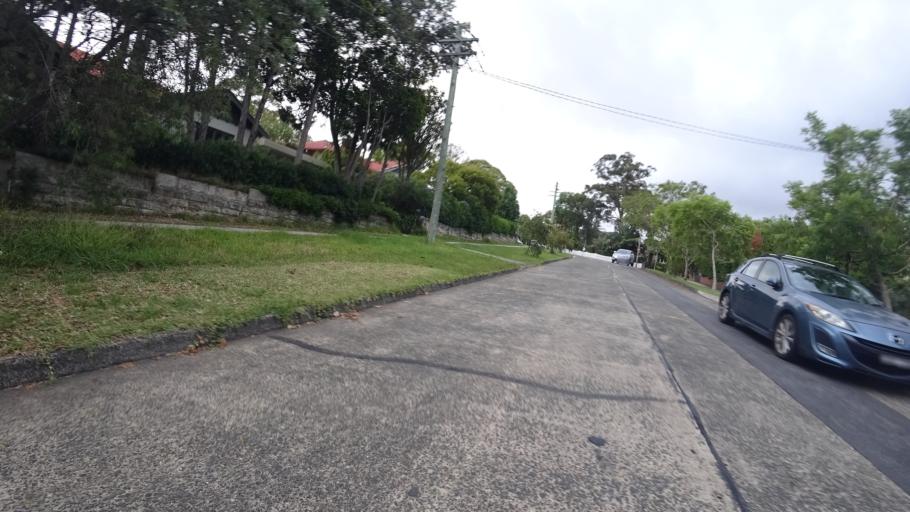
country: AU
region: New South Wales
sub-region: Willoughby
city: Chatswood
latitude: -33.8029
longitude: 151.1865
